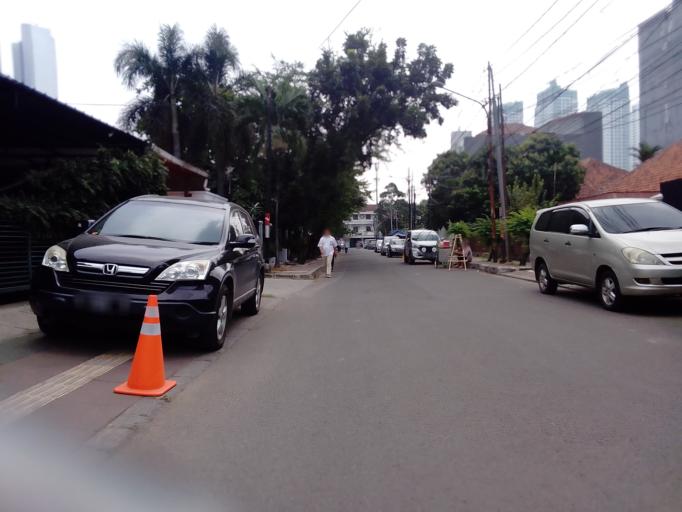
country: ID
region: Jakarta Raya
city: Jakarta
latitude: -6.2002
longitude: 106.8215
